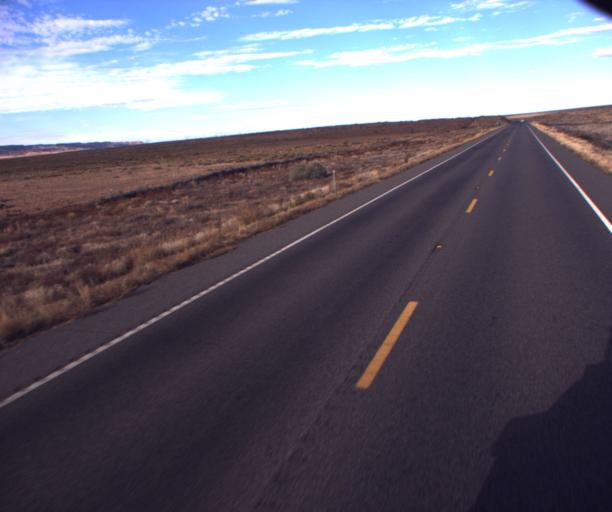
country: US
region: Arizona
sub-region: Apache County
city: Lukachukai
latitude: 36.9540
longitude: -109.2941
